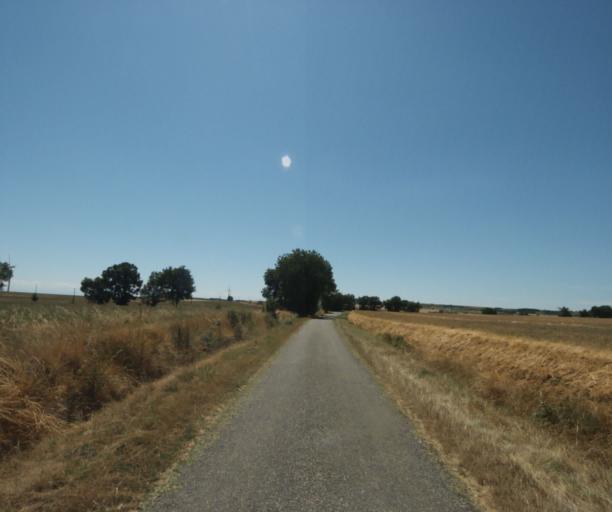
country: FR
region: Midi-Pyrenees
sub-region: Departement de la Haute-Garonne
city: Saint-Felix-Lauragais
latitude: 43.4693
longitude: 1.9105
